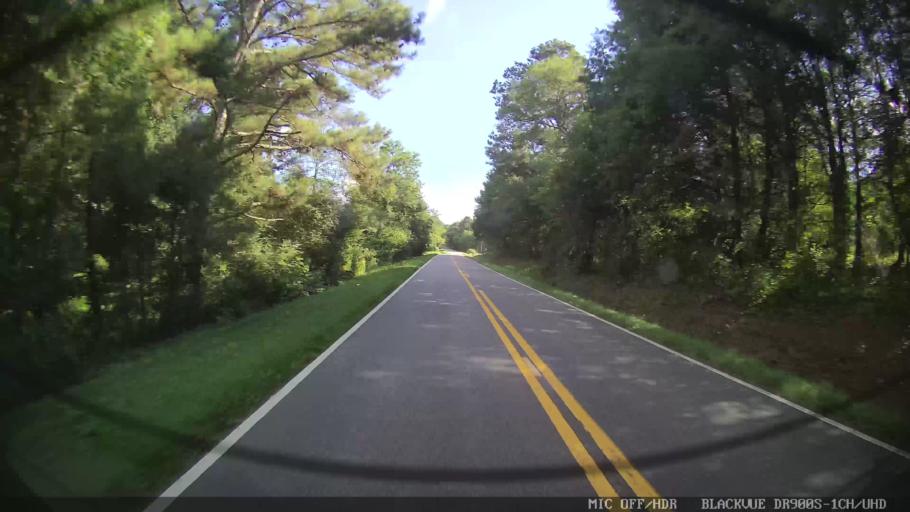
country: US
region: Georgia
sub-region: Bartow County
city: Euharlee
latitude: 34.1609
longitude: -84.9862
